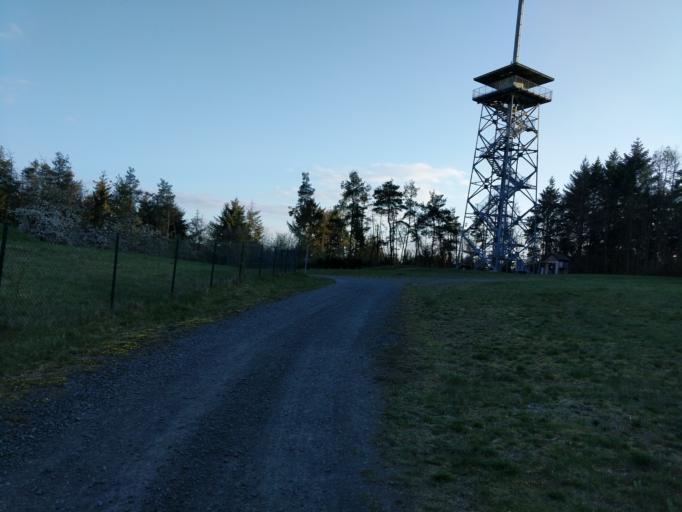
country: DE
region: Hesse
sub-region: Regierungsbezirk Giessen
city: Bad Endbach
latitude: 50.7610
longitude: 8.4901
